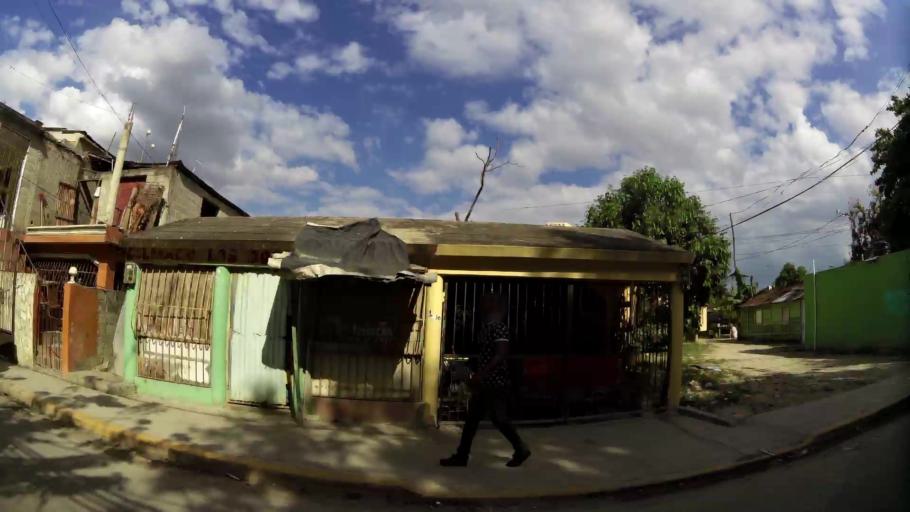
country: DO
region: Nacional
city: Ensanche Luperon
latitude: 18.5421
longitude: -69.8968
